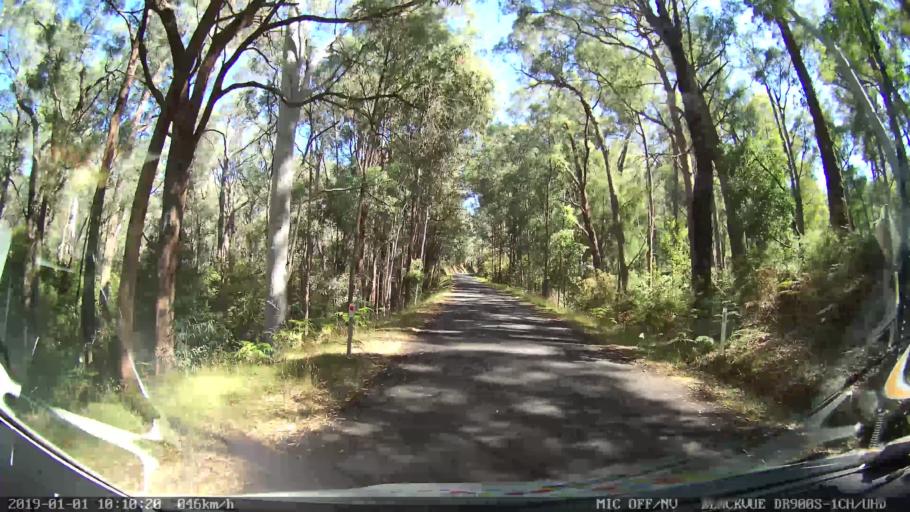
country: AU
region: New South Wales
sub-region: Snowy River
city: Jindabyne
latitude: -36.1420
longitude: 148.1583
